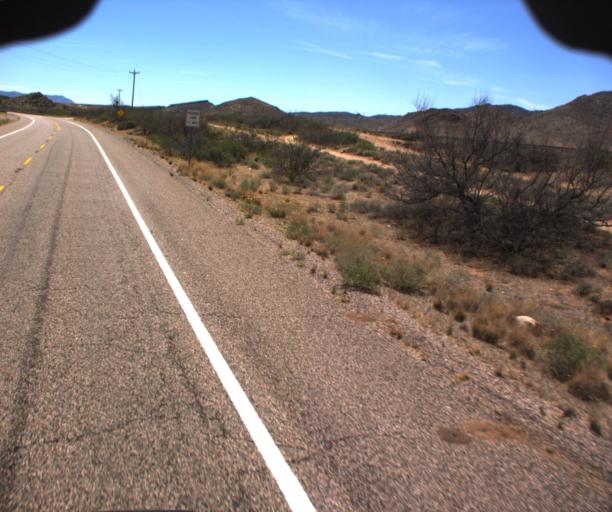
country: US
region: Arizona
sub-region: Mohave County
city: New Kingman-Butler
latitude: 35.3831
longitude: -113.7322
